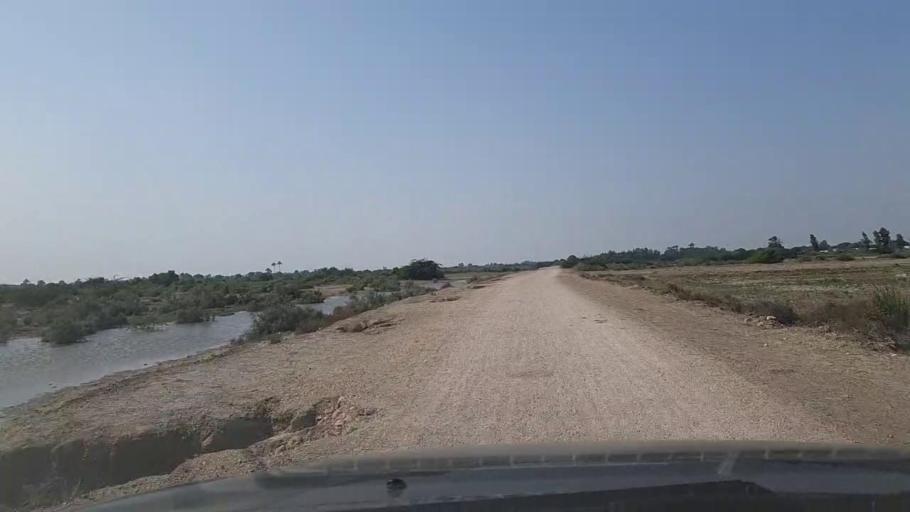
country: PK
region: Sindh
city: Mirpur Sakro
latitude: 24.4060
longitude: 67.6835
